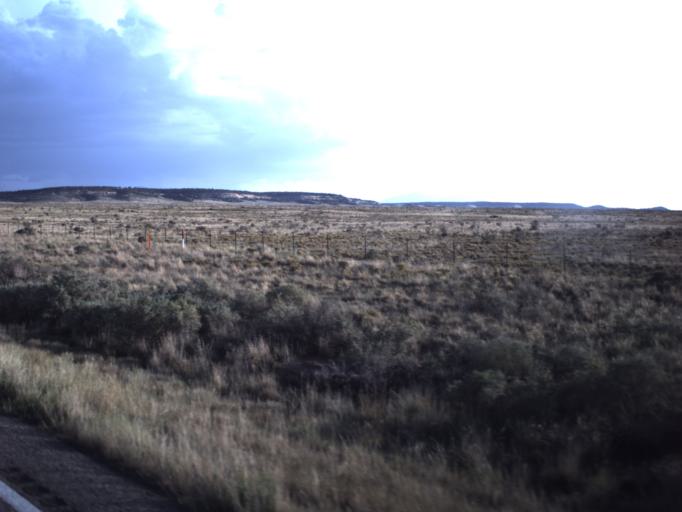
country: US
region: Utah
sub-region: San Juan County
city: Monticello
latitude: 38.1589
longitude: -109.3761
